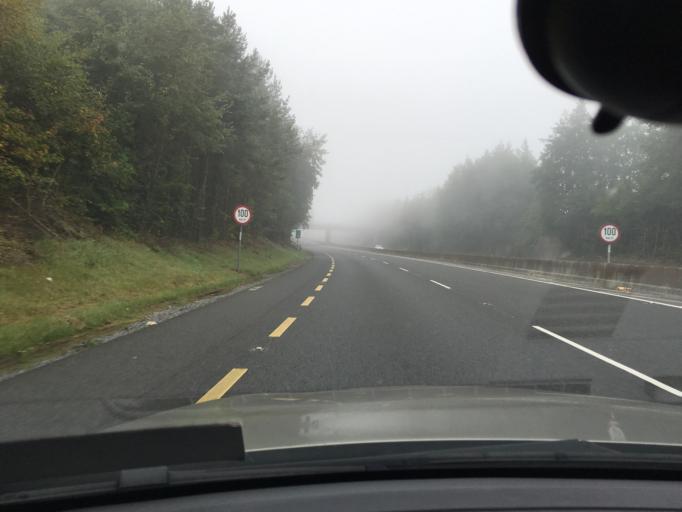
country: IE
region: Leinster
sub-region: An Iarmhi
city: Athlone
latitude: 53.4241
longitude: -7.9751
